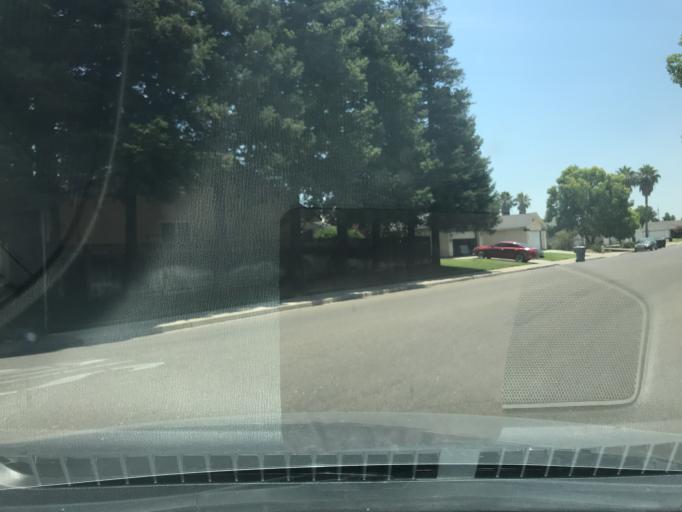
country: US
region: California
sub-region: Merced County
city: Atwater
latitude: 37.3641
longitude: -120.6008
